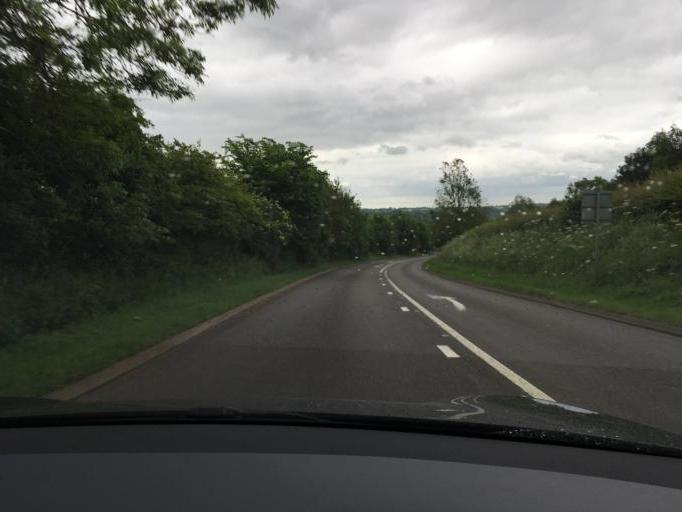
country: GB
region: England
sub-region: Staffordshire
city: Mayfield
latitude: 53.0148
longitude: -1.7770
